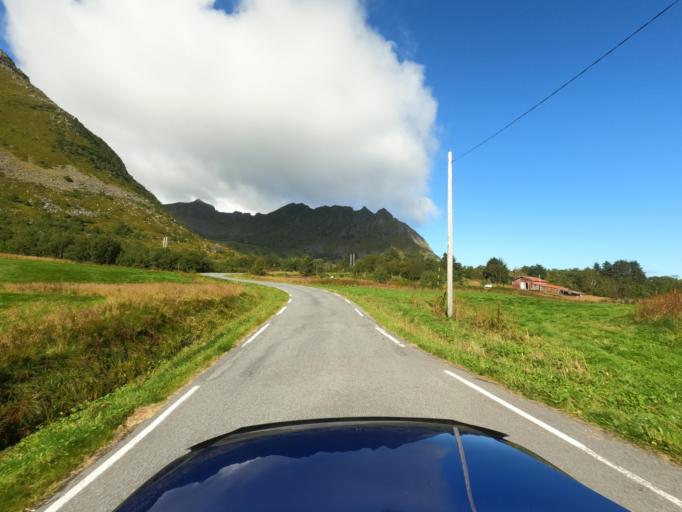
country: NO
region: Nordland
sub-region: Vagan
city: Kabelvag
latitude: 68.2847
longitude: 14.2652
